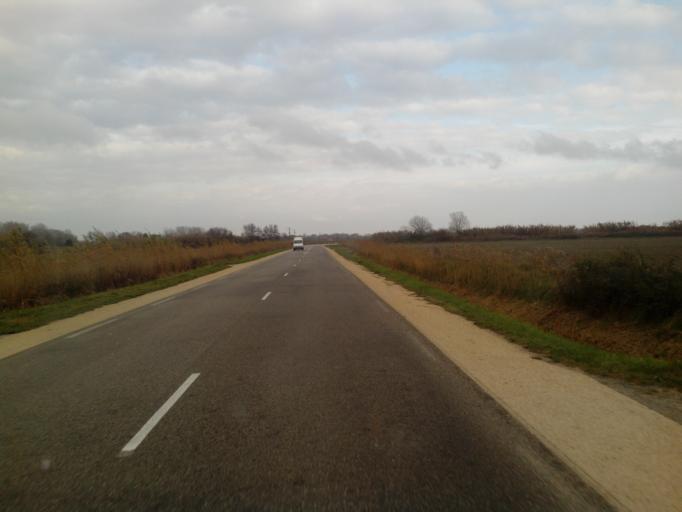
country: FR
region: Provence-Alpes-Cote d'Azur
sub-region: Departement des Bouches-du-Rhone
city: Saintes-Maries-de-la-Mer
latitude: 43.5487
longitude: 4.3777
